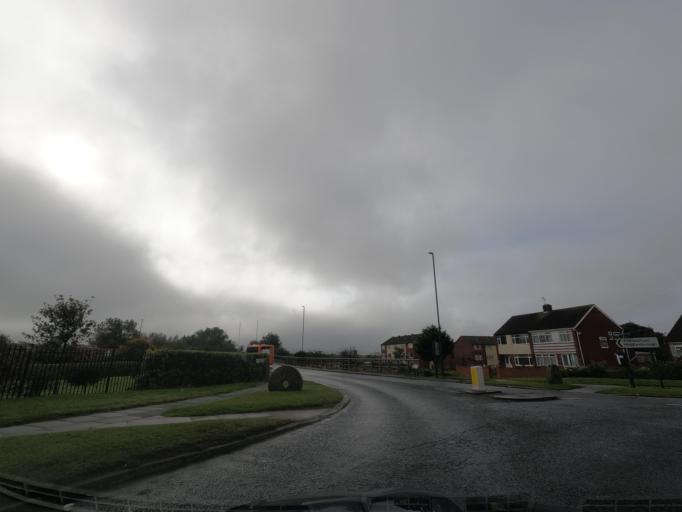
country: GB
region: England
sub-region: Redcar and Cleveland
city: Redcar
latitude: 54.6166
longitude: -1.0850
